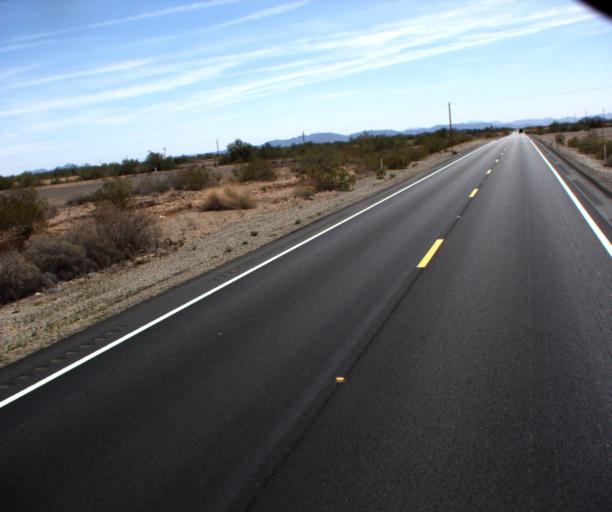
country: US
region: Arizona
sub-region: Yuma County
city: Wellton
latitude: 32.9966
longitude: -114.2866
